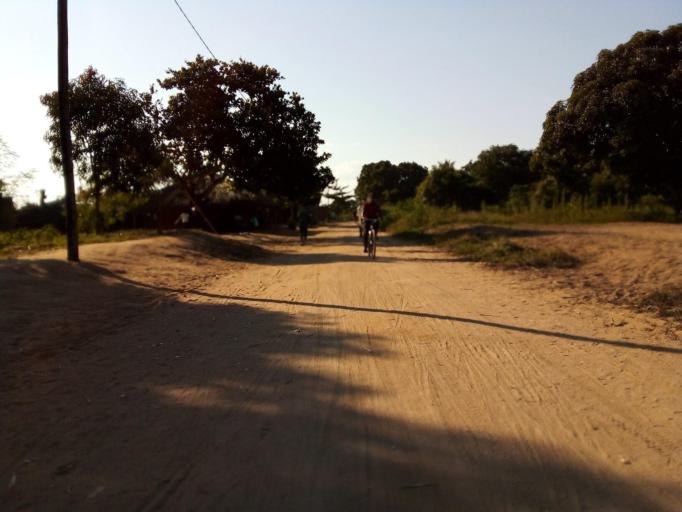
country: MZ
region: Zambezia
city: Quelimane
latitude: -17.5571
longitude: 36.6985
